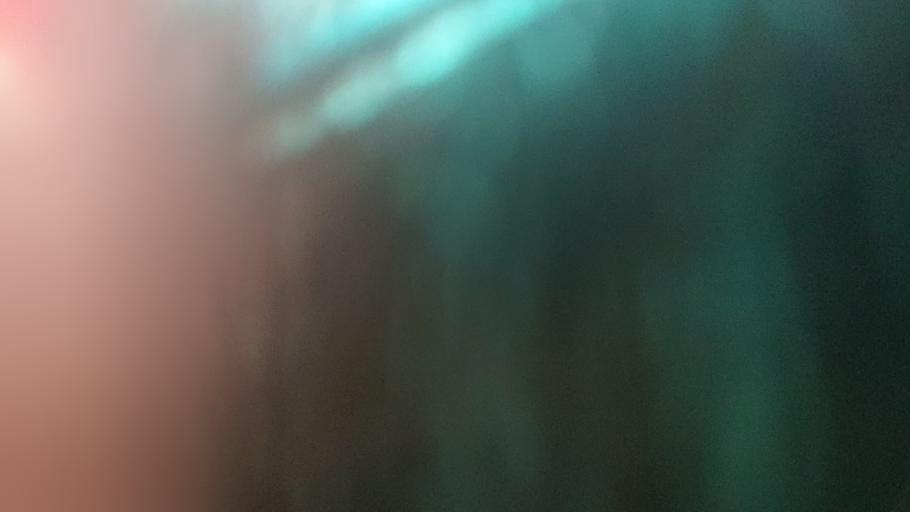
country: TW
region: Taiwan
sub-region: Chiayi
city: Taibao
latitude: 23.7063
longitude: 120.1821
